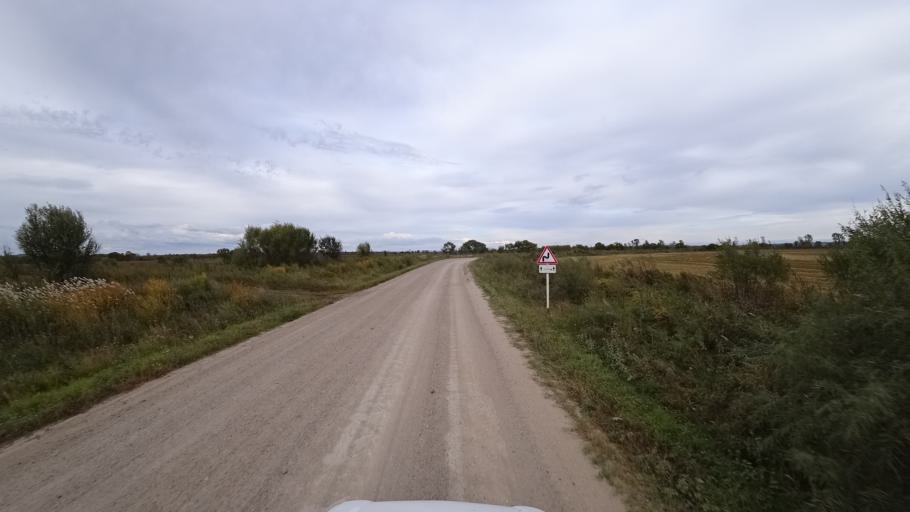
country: RU
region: Amur
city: Arkhara
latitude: 49.3753
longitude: 130.1536
